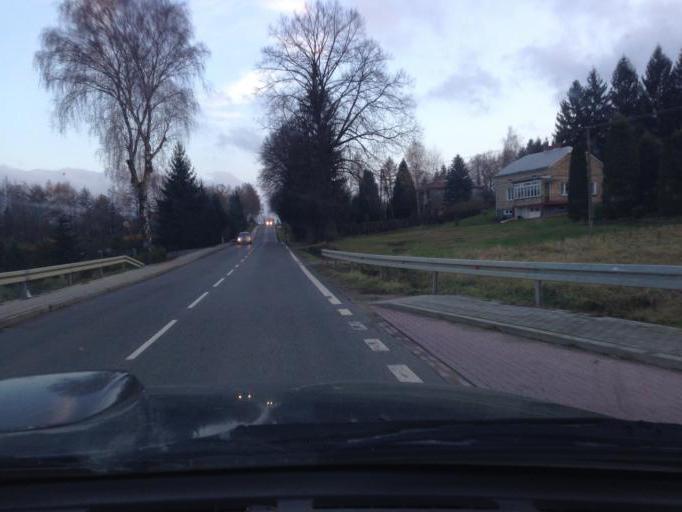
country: PL
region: Subcarpathian Voivodeship
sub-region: Powiat jasielski
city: Osiek Jasielski
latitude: 49.6415
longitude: 21.5188
